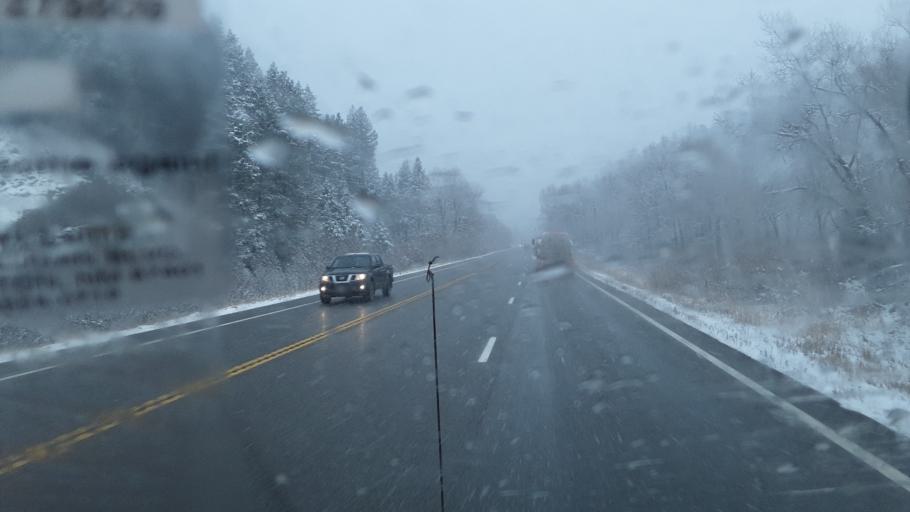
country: US
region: Colorado
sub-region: La Plata County
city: Bayfield
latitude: 37.2296
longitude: -107.4142
